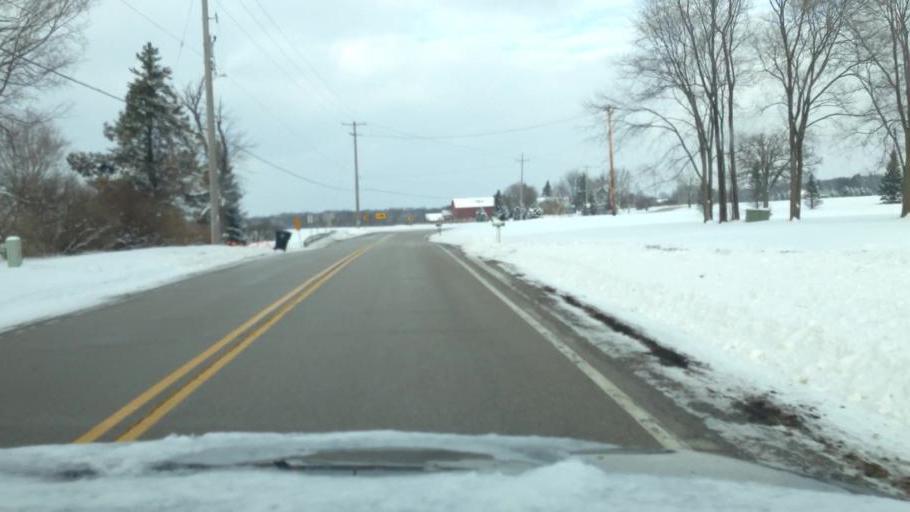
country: US
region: Wisconsin
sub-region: Waukesha County
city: North Prairie
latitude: 42.8997
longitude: -88.4151
